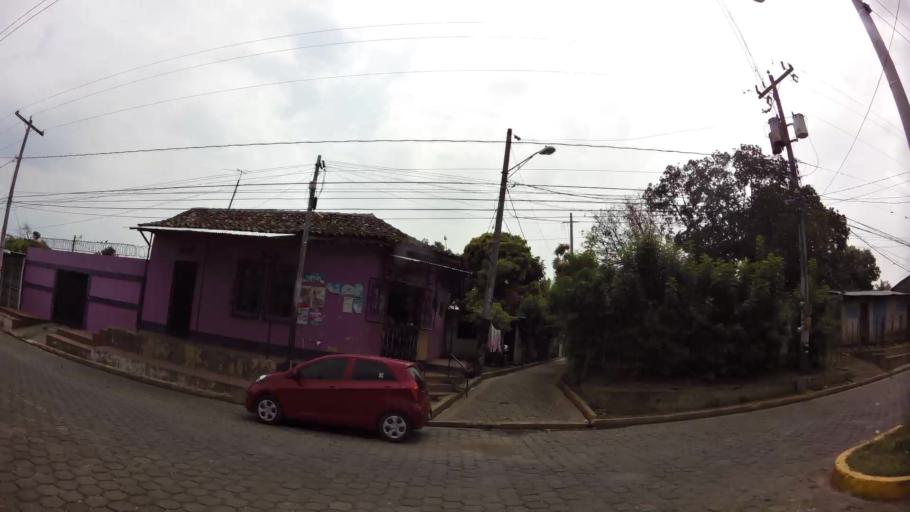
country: NI
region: Granada
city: Diria
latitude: 11.8819
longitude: -86.0539
